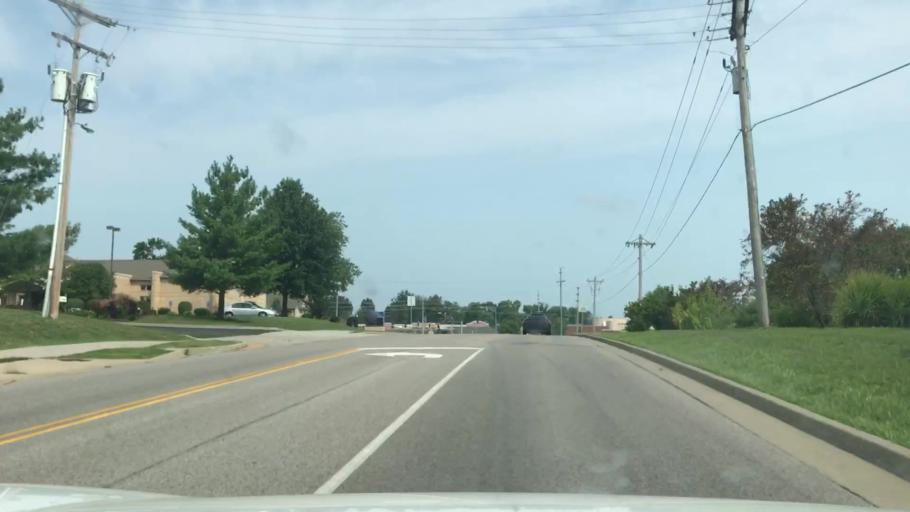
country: US
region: Missouri
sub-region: Saint Charles County
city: Cottleville
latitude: 38.7258
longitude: -90.6435
